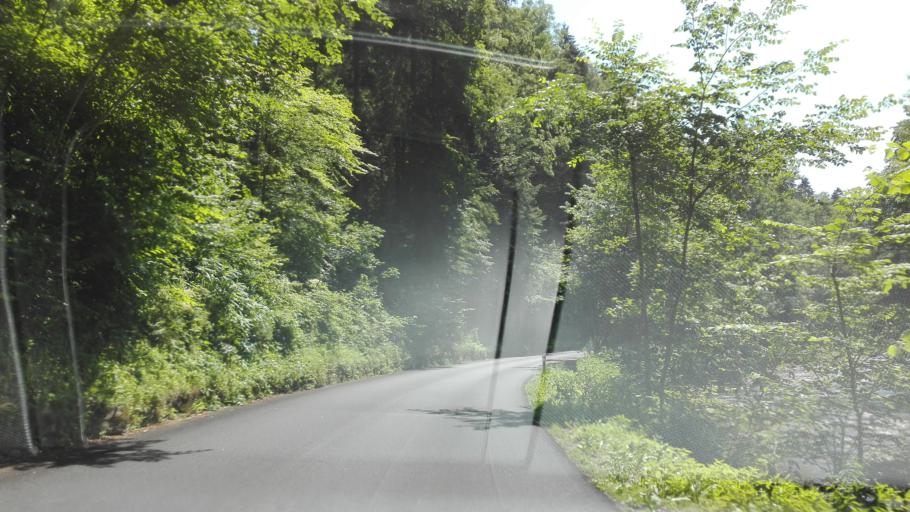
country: AT
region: Upper Austria
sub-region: Politischer Bezirk Rohrbach
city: Kleinzell im Muehlkreis
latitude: 48.3806
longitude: 13.9097
